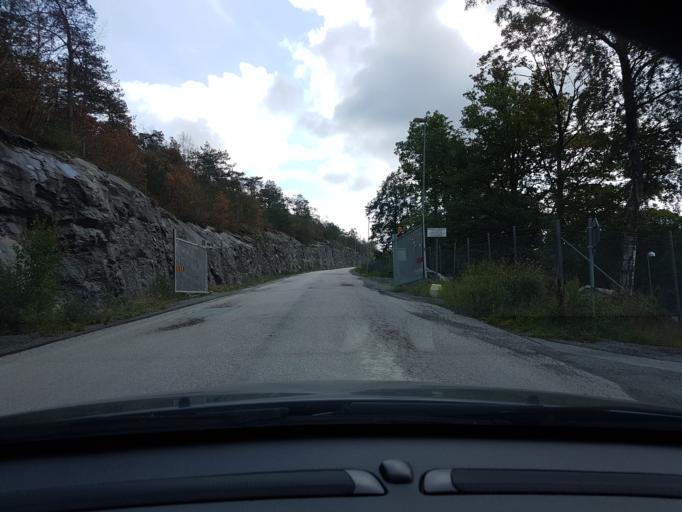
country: SE
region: Vaestra Goetaland
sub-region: Ale Kommun
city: Nodinge-Nol
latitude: 57.8705
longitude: 12.0349
